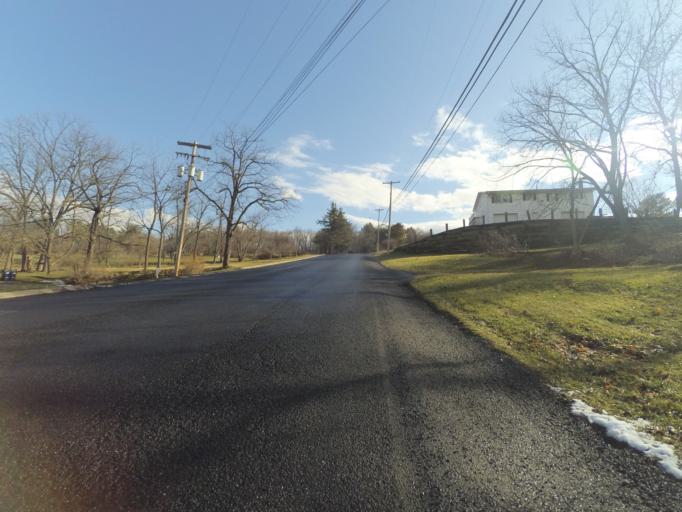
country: US
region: Pennsylvania
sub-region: Centre County
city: Lemont
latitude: 40.8088
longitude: -77.8333
